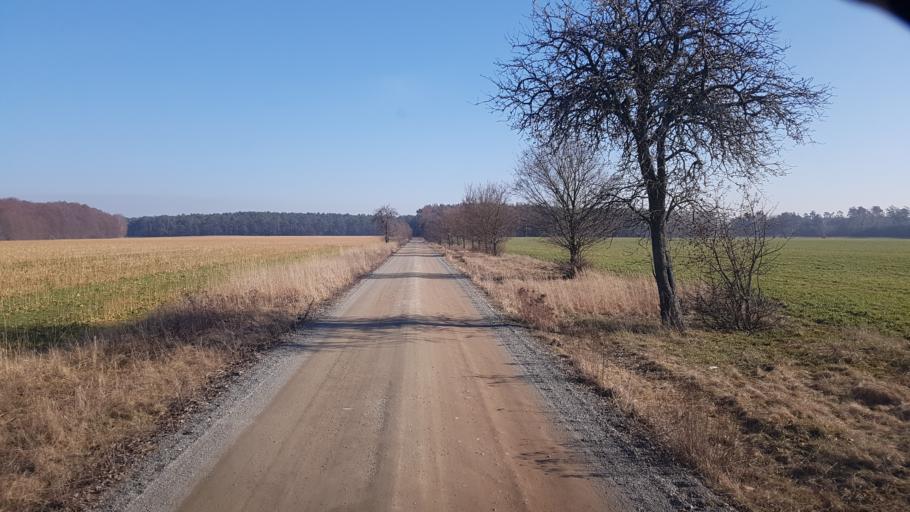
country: DE
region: Brandenburg
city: Lebusa
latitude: 51.8196
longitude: 13.3706
